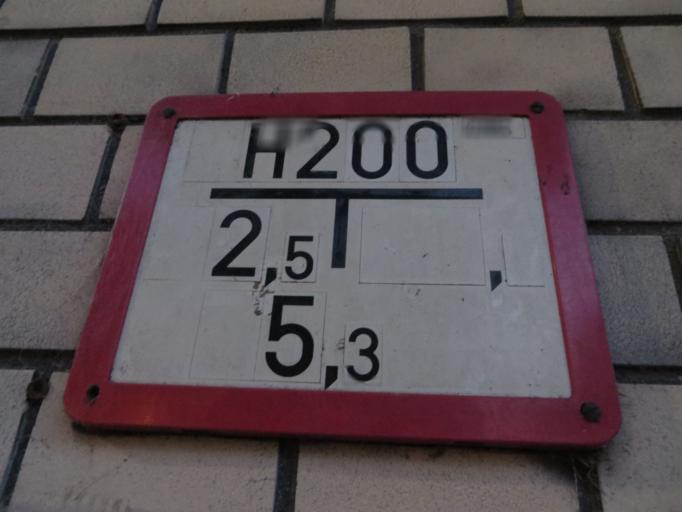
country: DE
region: North Rhine-Westphalia
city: Witten
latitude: 51.4337
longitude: 7.3406
